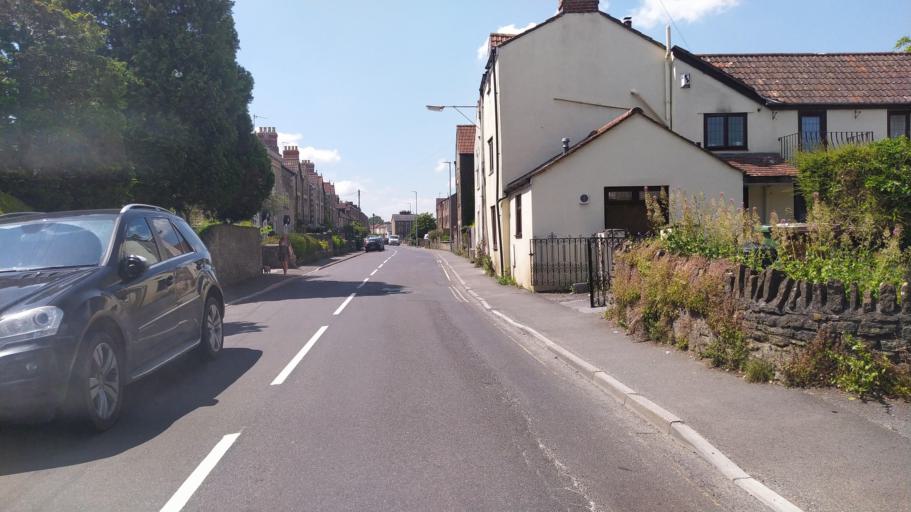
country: GB
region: England
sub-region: Somerset
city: Frome
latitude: 51.2251
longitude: -2.3267
